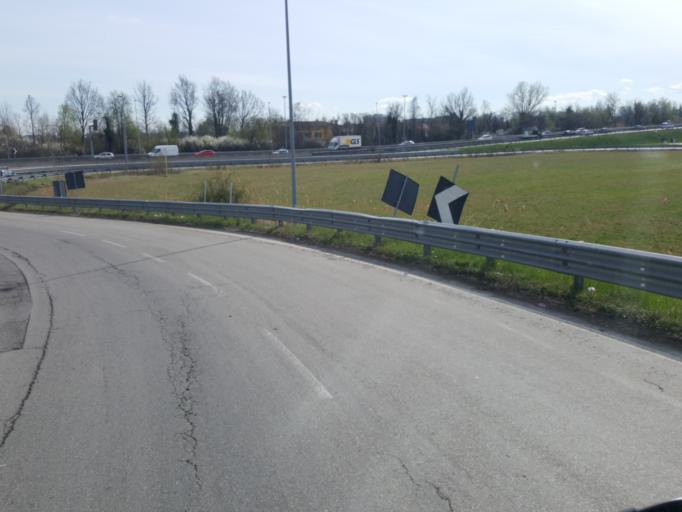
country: IT
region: Emilia-Romagna
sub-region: Provincia di Modena
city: Modena
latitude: 44.6485
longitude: 10.9621
